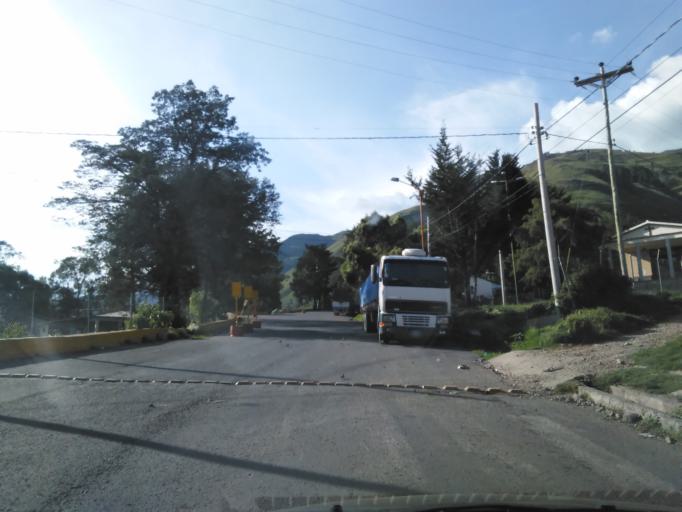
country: BO
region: Cochabamba
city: Cochabamba
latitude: -17.3303
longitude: -66.1845
